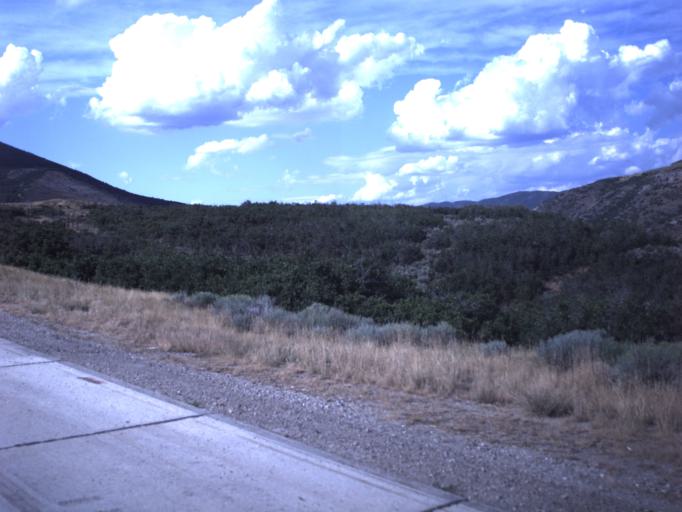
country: US
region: Utah
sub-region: Wasatch County
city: Heber
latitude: 40.5753
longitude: -111.4343
